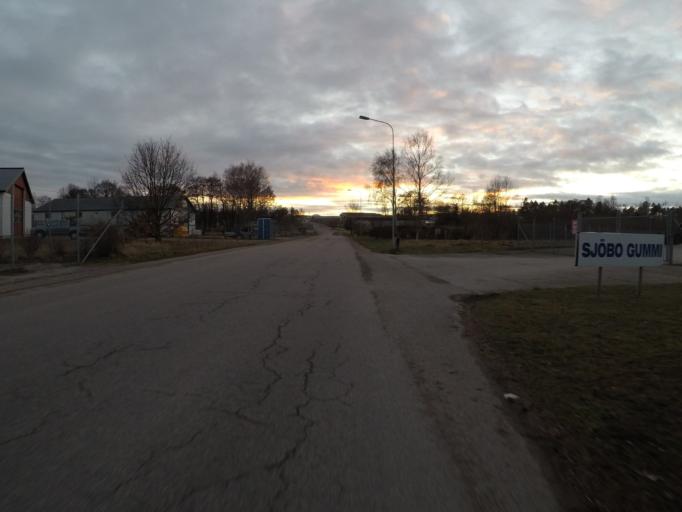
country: SE
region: Skane
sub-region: Sjobo Kommun
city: Sjoebo
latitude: 55.6402
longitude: 13.6867
